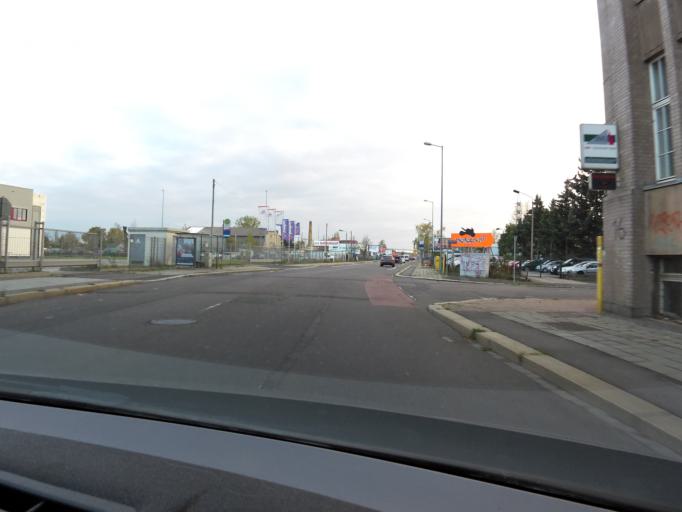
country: DE
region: Saxony
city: Leipzig
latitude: 51.3480
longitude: 12.3012
